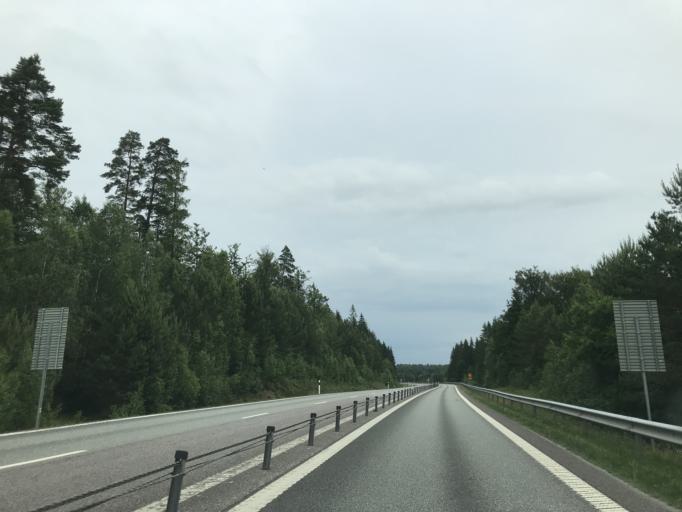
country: SE
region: Skane
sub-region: Hassleholms Kommun
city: Hastveda
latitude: 56.2869
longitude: 13.9984
